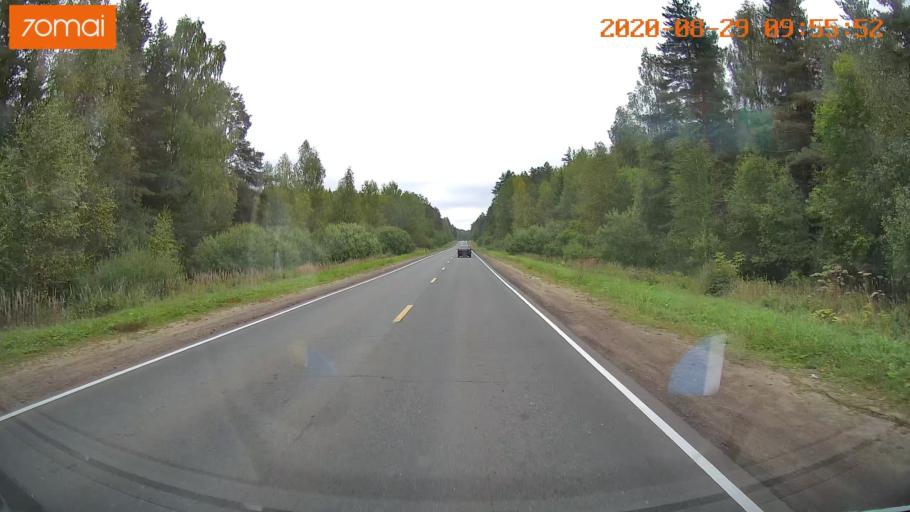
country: RU
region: Ivanovo
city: Zarechnyy
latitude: 57.4216
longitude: 42.2745
